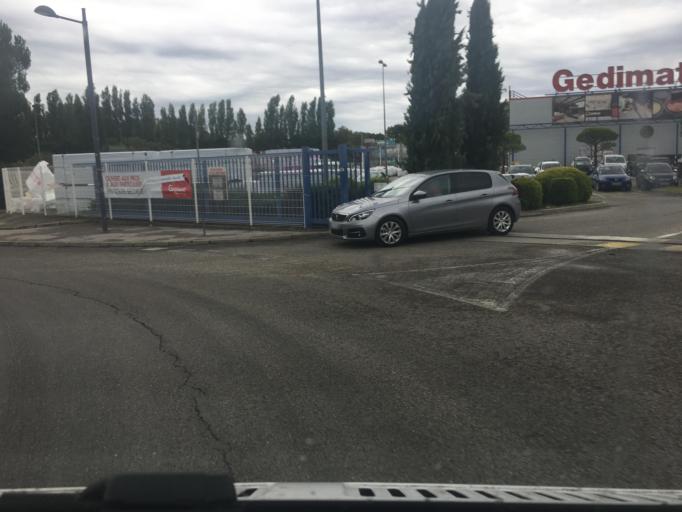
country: FR
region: Languedoc-Roussillon
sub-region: Departement du Gard
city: Uzes
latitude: 43.9895
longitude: 4.4284
